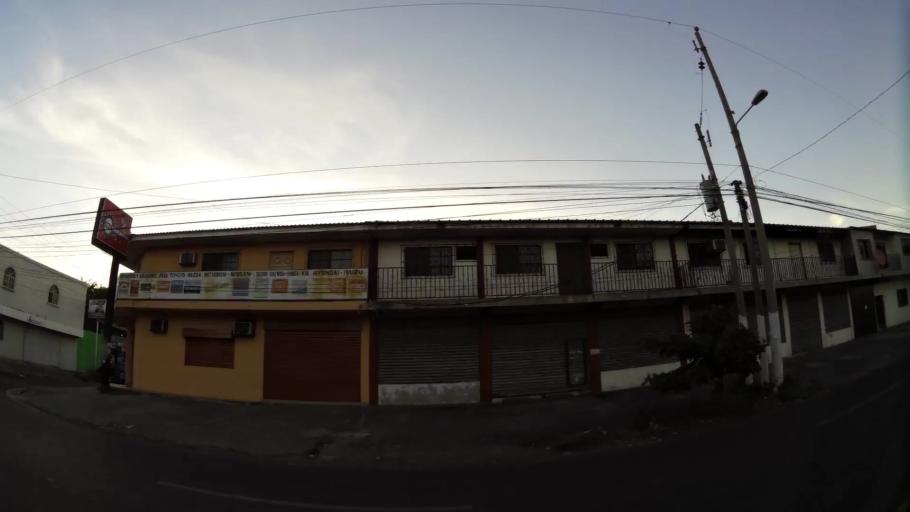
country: SV
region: San Miguel
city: San Miguel
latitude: 13.4911
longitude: -88.1716
